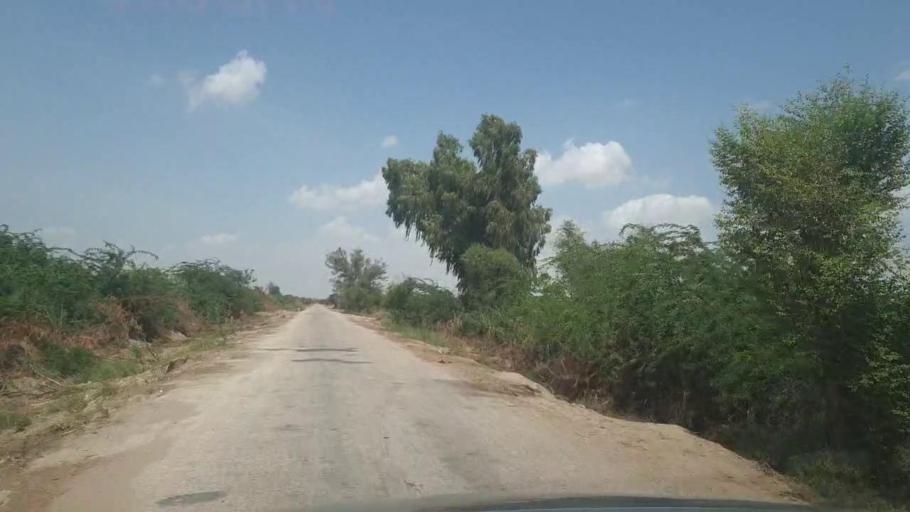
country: PK
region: Sindh
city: Kot Diji
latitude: 27.2152
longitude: 69.0336
